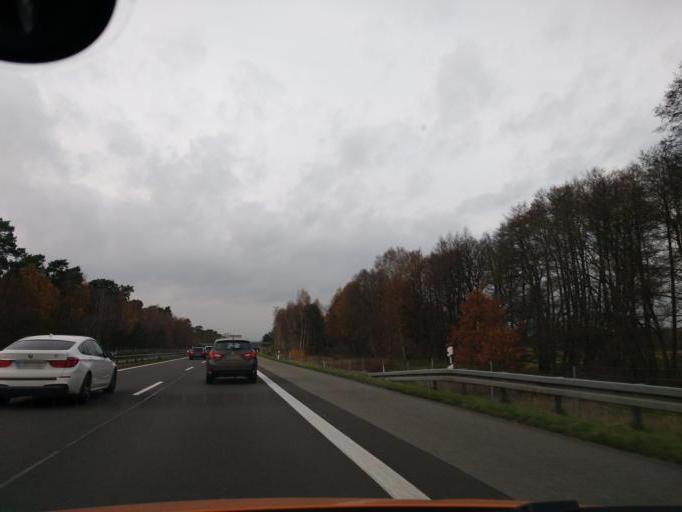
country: DE
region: Brandenburg
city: Wittstock
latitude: 53.0514
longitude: 12.5406
